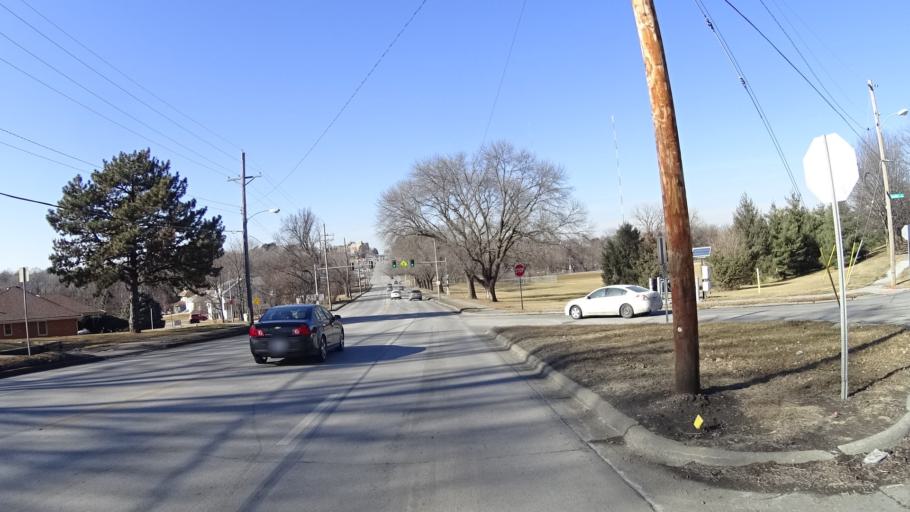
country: US
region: Nebraska
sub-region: Douglas County
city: Omaha
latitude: 41.2939
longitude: -96.0167
